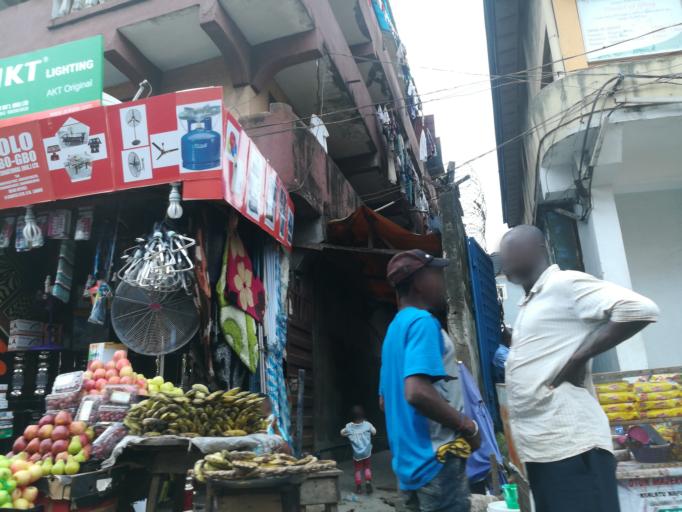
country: NG
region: Lagos
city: Ebute Metta
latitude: 6.4817
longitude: 3.3838
